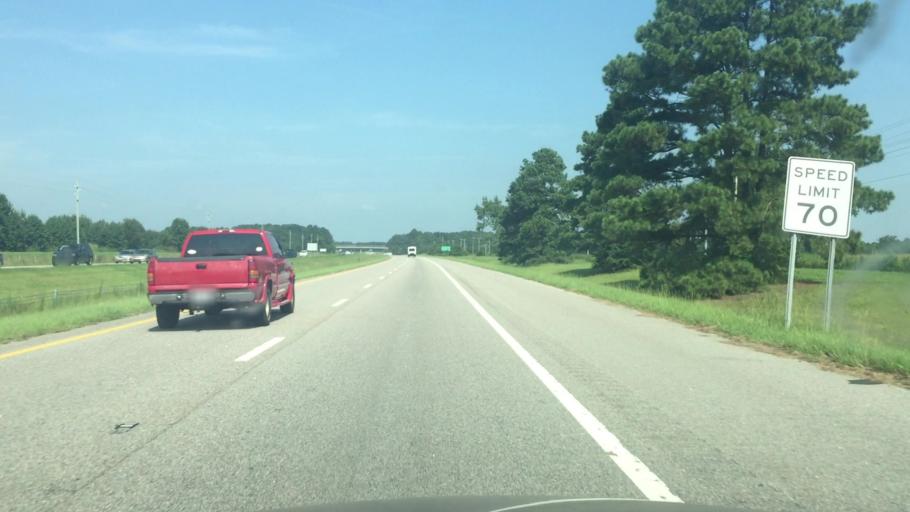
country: US
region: North Carolina
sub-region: Robeson County
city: Lumberton
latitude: 34.5855
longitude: -79.0581
